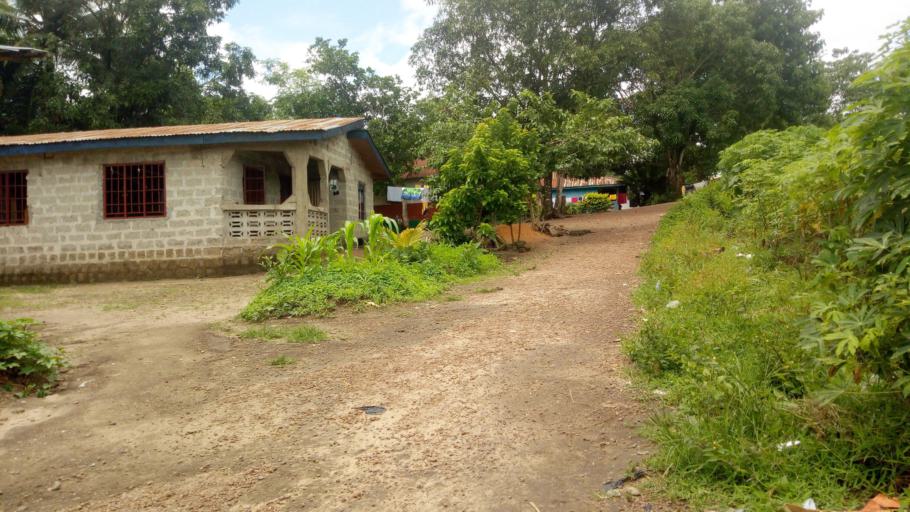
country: SL
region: Northern Province
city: Magburaka
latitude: 8.7150
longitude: -11.9556
